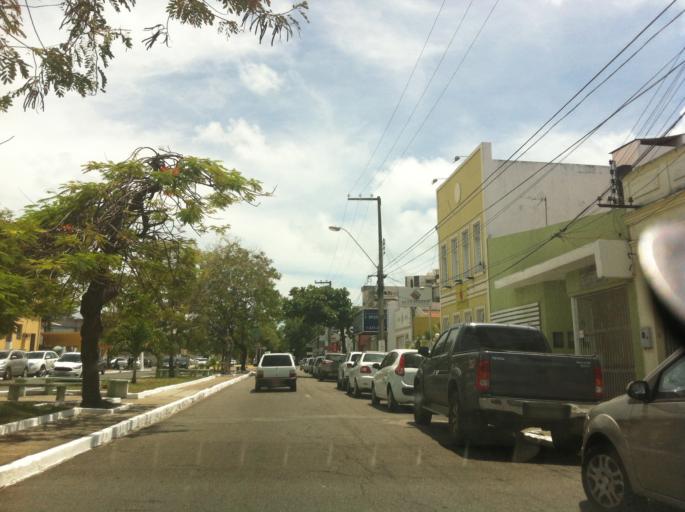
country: BR
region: Alagoas
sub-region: Maceio
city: Maceio
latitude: -9.6713
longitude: -35.7173
